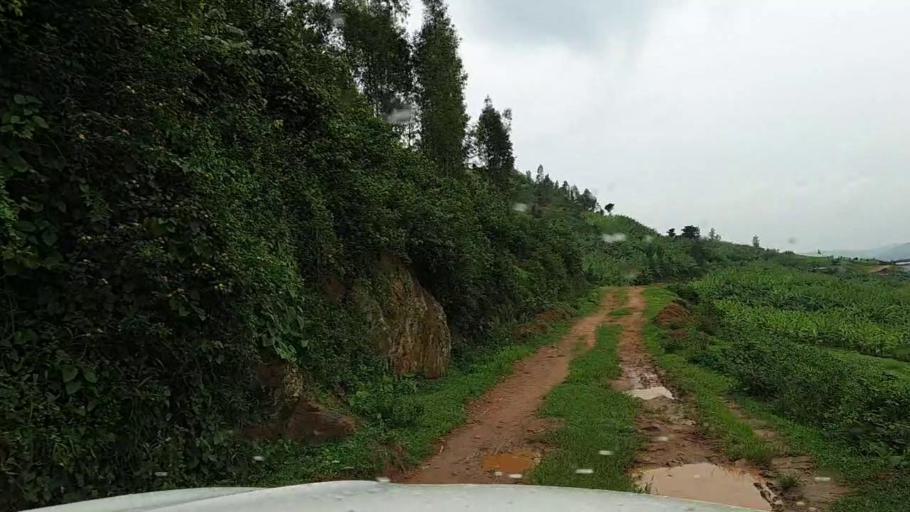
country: RW
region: Kigali
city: Kigali
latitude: -1.9061
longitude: 29.9573
